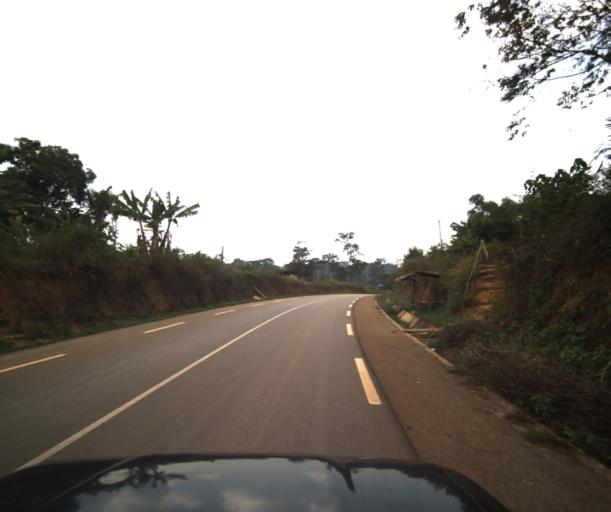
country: CM
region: Centre
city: Akono
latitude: 3.6141
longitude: 11.3132
